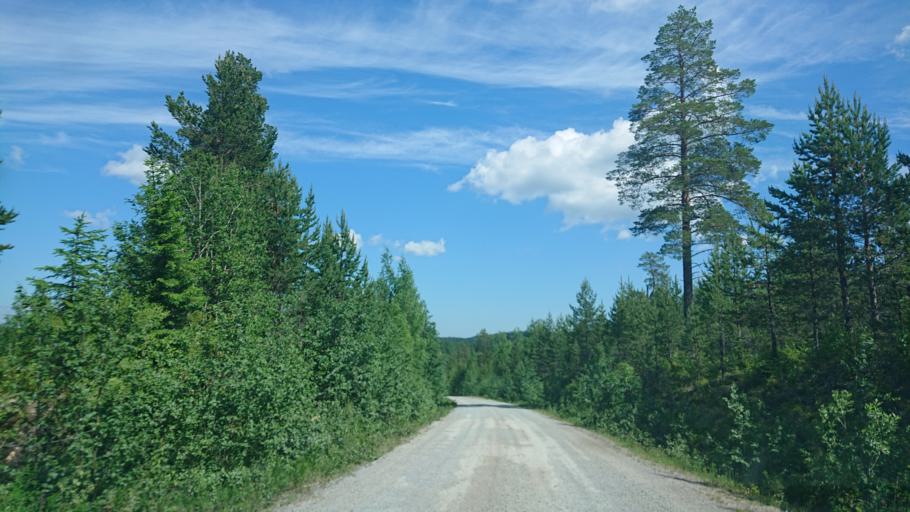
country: SE
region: Vaesternorrland
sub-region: Solleftea Kommun
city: Solleftea
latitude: 62.9312
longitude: 17.0981
